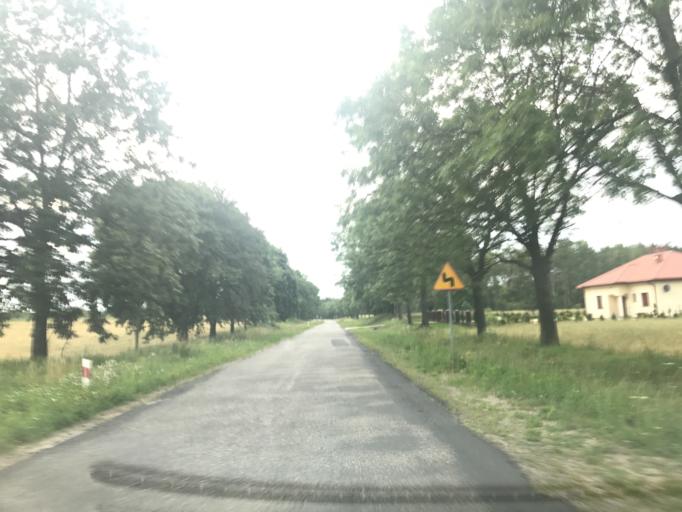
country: PL
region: Kujawsko-Pomorskie
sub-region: Powiat lipnowski
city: Lipno
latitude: 52.7960
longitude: 19.2063
